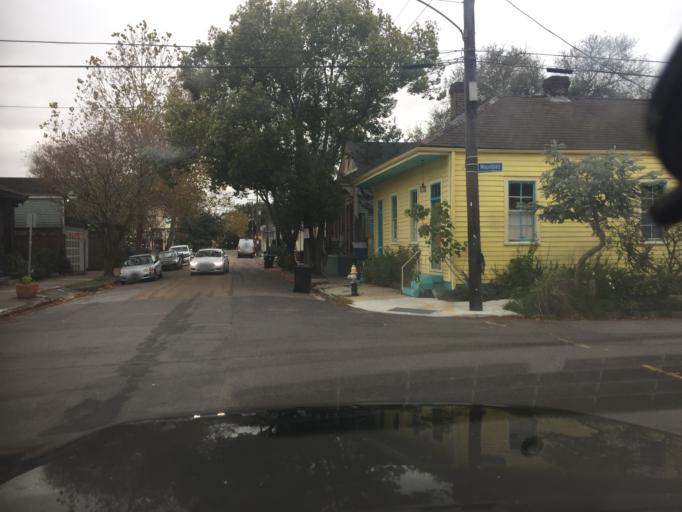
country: US
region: Louisiana
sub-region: Orleans Parish
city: New Orleans
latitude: 29.9811
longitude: -90.0833
